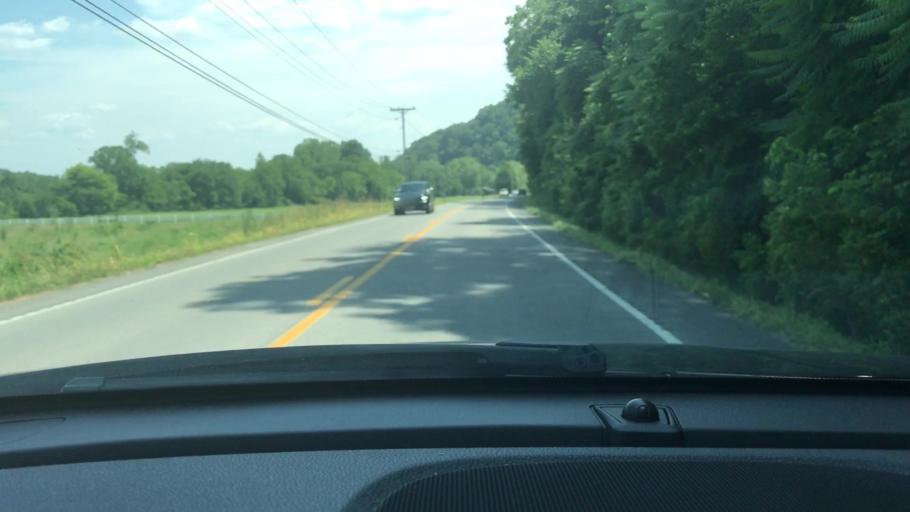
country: US
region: Tennessee
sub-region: Sumner County
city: Shackle Island
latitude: 36.3992
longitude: -86.6299
